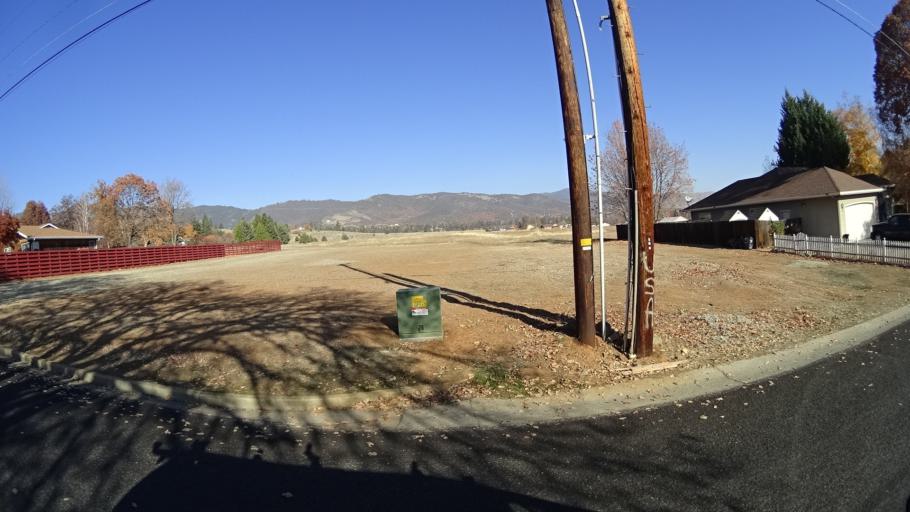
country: US
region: California
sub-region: Siskiyou County
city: Yreka
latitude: 41.7237
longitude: -122.6480
